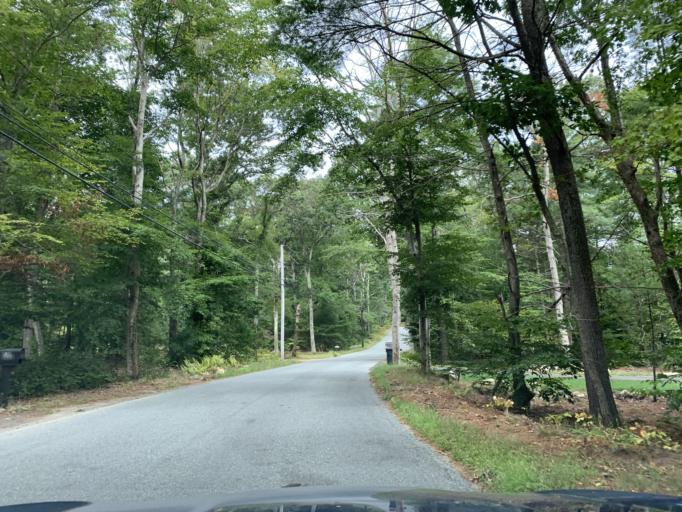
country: US
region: Rhode Island
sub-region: Kent County
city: West Greenwich
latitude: 41.5725
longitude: -71.6222
